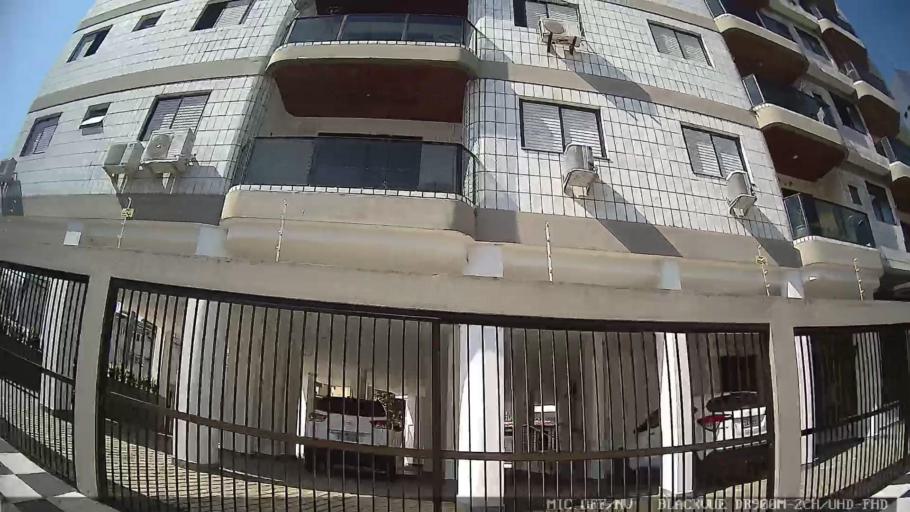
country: BR
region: Sao Paulo
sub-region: Guaruja
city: Guaruja
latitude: -24.0112
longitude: -46.2737
